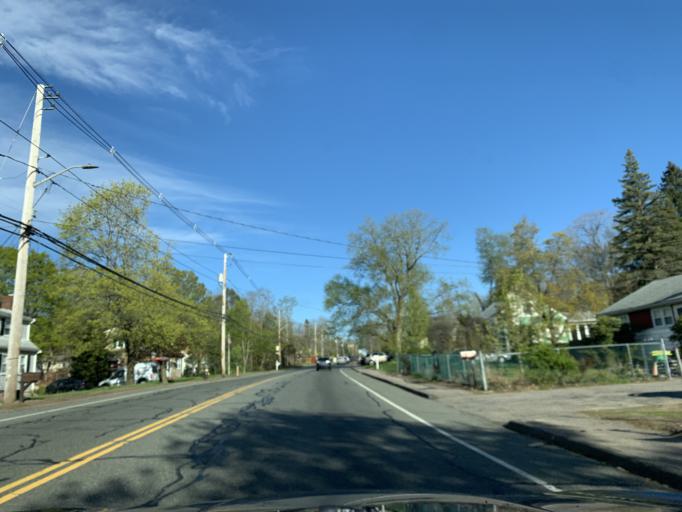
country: US
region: Massachusetts
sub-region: Norfolk County
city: Stoughton
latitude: 42.1285
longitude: -71.0774
